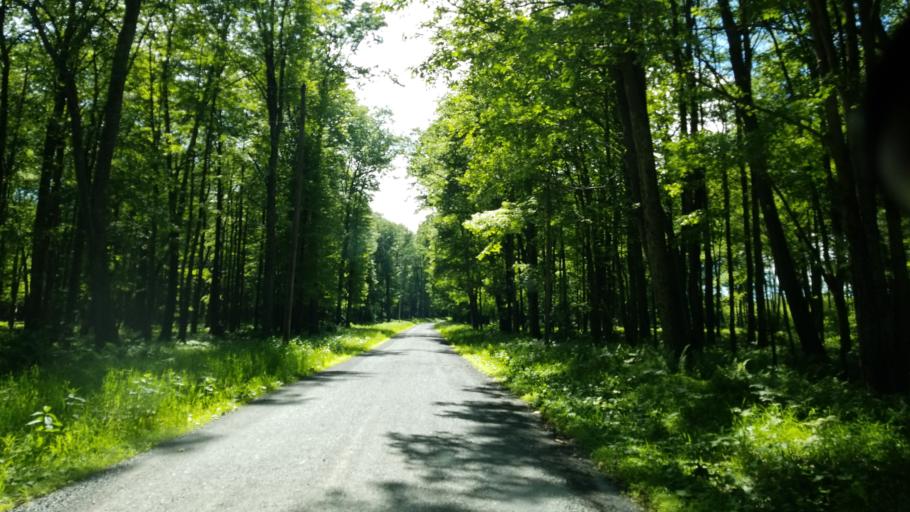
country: US
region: Pennsylvania
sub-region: Clearfield County
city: Clearfield
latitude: 41.1820
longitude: -78.4474
